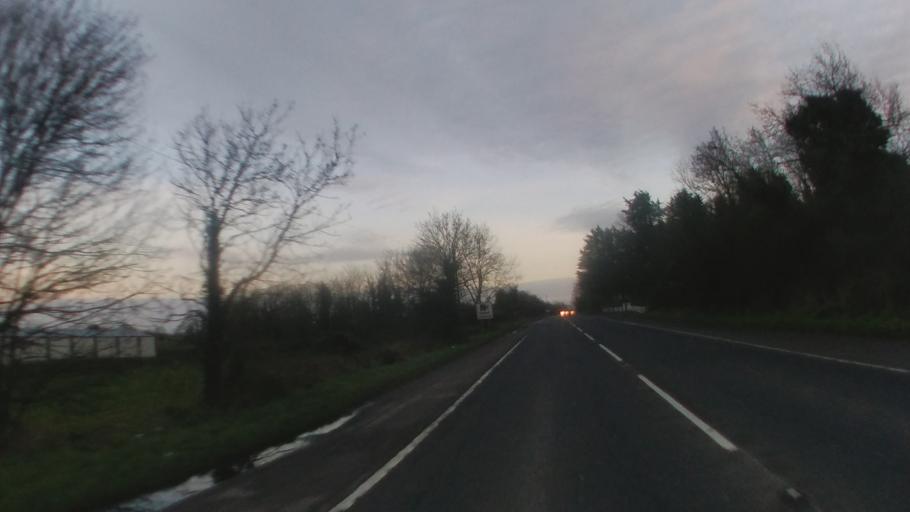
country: GB
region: Northern Ireland
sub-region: Armagh District
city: Tandragee
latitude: 54.2942
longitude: -6.5111
